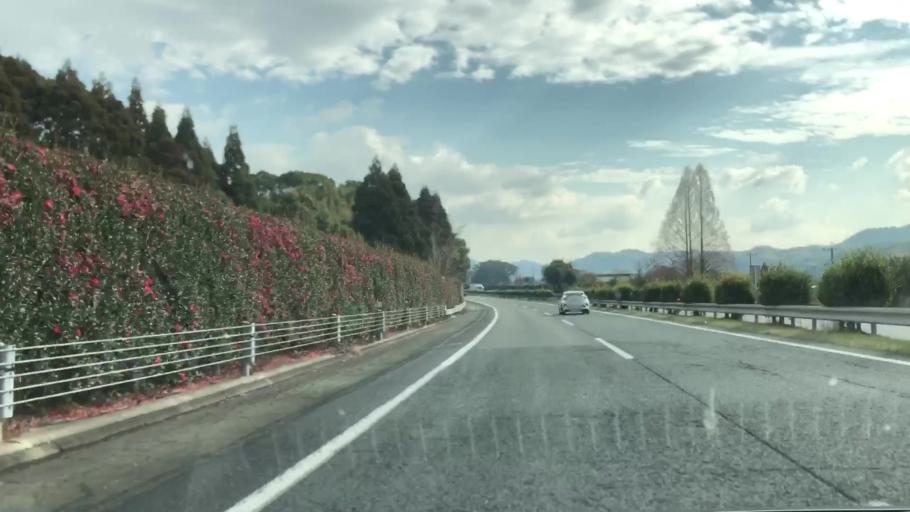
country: JP
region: Fukuoka
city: Setakamachi-takayanagi
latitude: 33.1231
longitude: 130.5196
